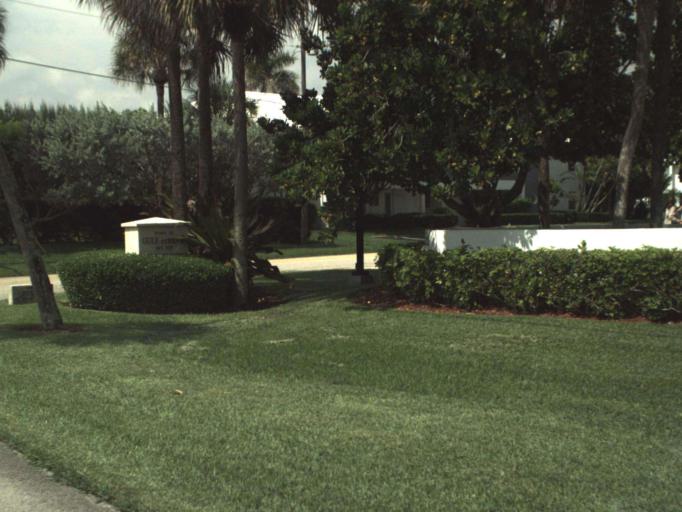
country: US
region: Florida
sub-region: Palm Beach County
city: Ocean Ridge
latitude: 26.5006
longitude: -80.0530
